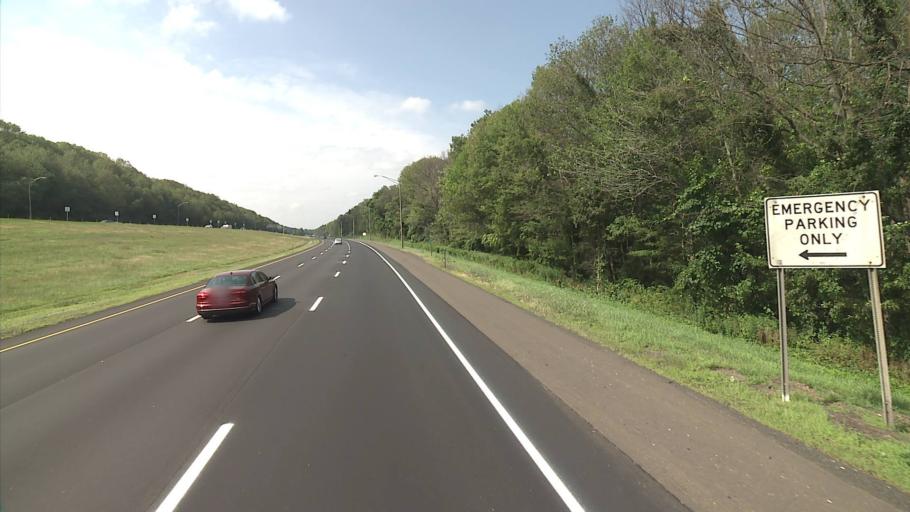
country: US
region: Connecticut
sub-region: New Haven County
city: Wallingford Center
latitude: 41.4196
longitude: -72.8279
